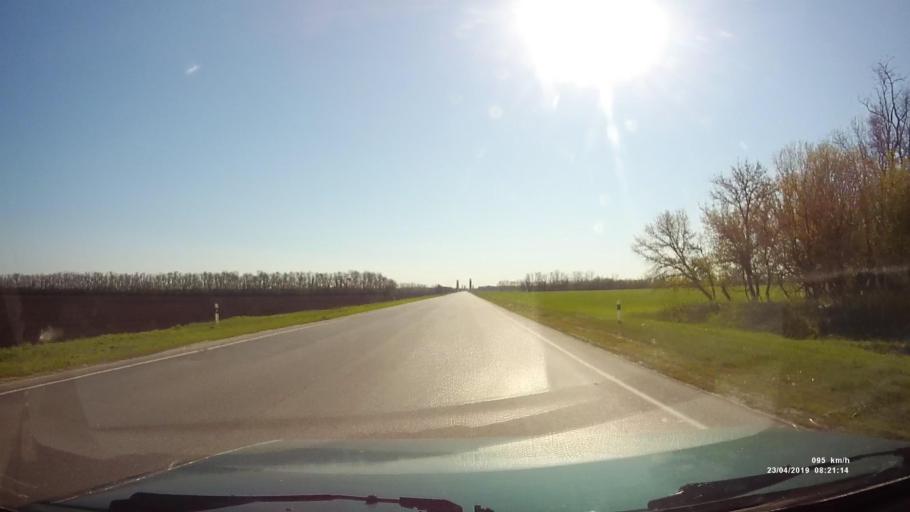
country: RU
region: Rostov
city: Tselina
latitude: 46.5354
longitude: 40.8861
